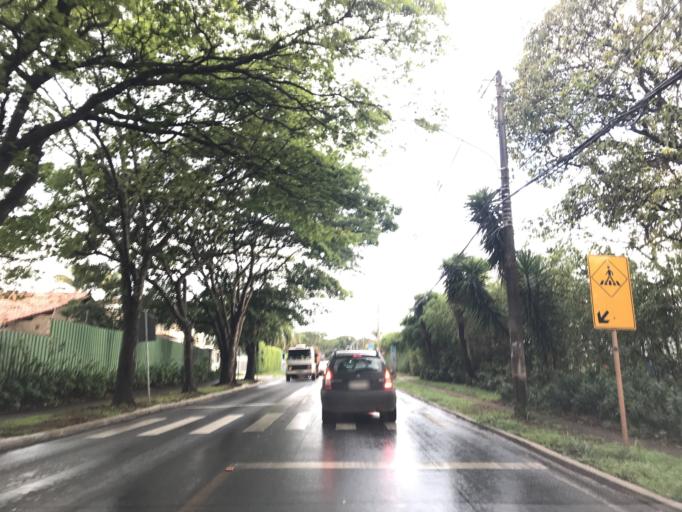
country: BR
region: Federal District
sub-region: Brasilia
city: Brasilia
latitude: -15.8453
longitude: -47.8907
